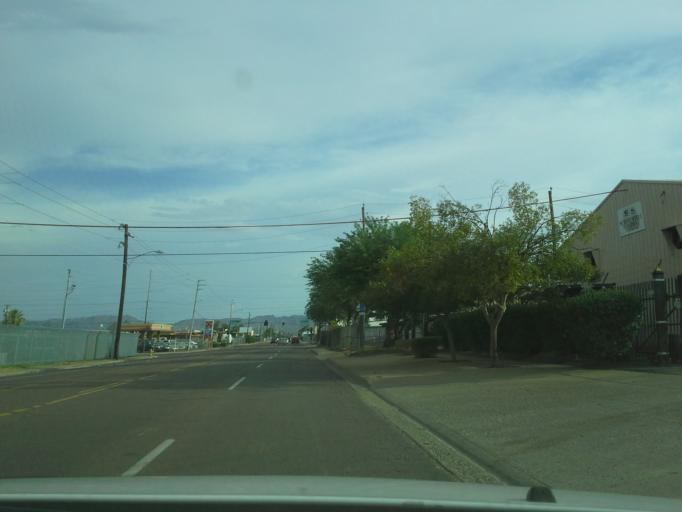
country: US
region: Arizona
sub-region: Maricopa County
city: Phoenix
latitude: 33.4432
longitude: -112.1002
